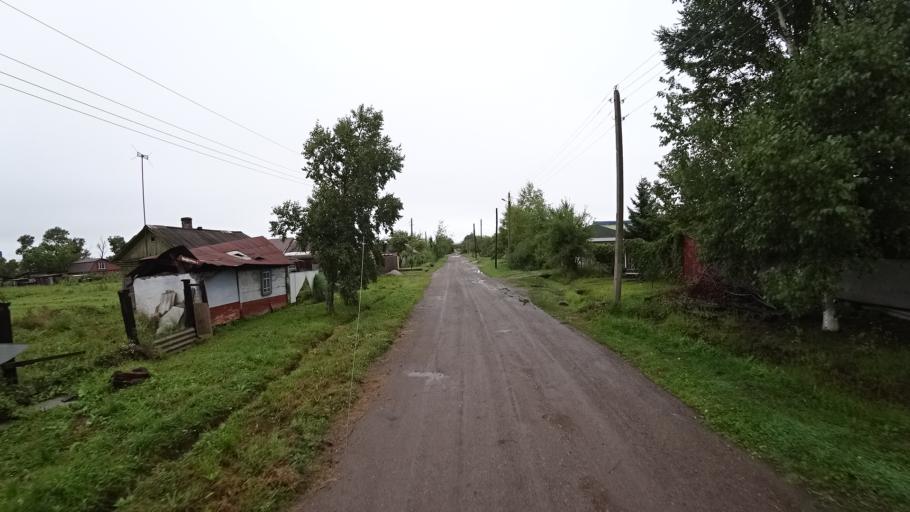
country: RU
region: Primorskiy
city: Monastyrishche
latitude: 44.2075
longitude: 132.4518
